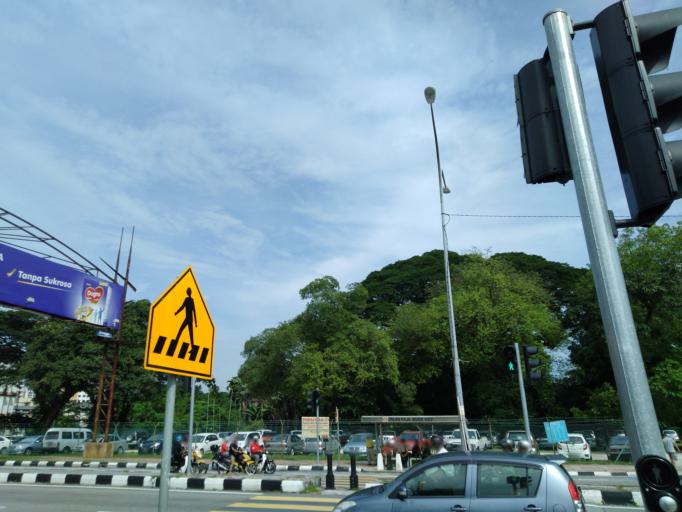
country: MY
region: Perak
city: Ipoh
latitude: 4.6019
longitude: 101.0865
